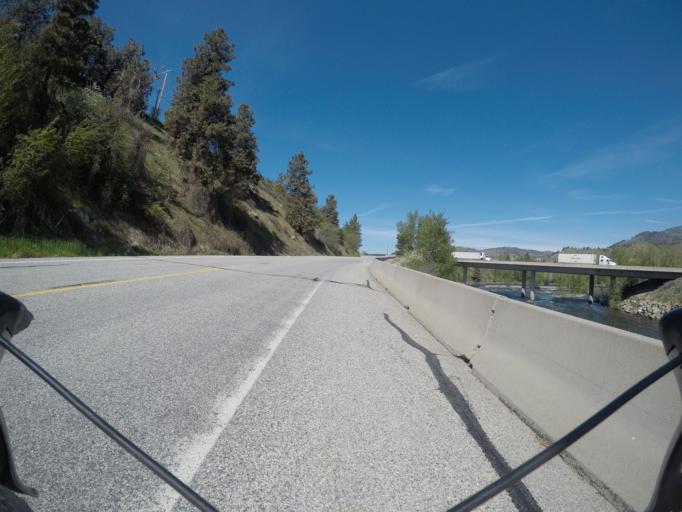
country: US
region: Washington
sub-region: Chelan County
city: Cashmere
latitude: 47.5342
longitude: -120.5506
